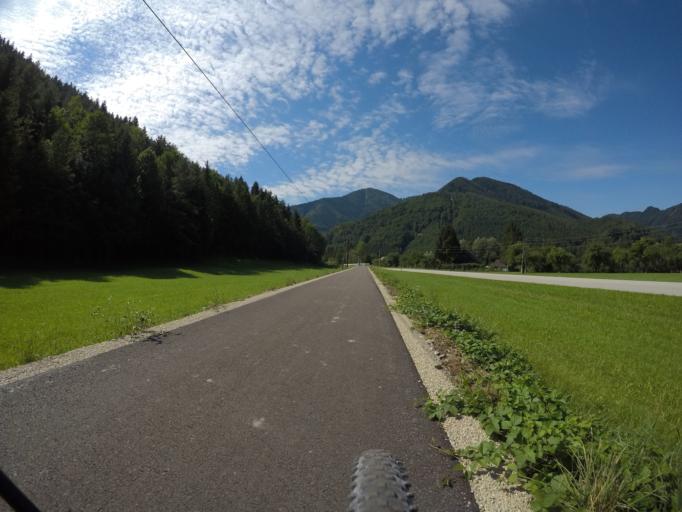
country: AT
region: Lower Austria
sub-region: Politischer Bezirk Amstetten
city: Hollenstein an der Ybbs
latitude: 47.8372
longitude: 14.7527
